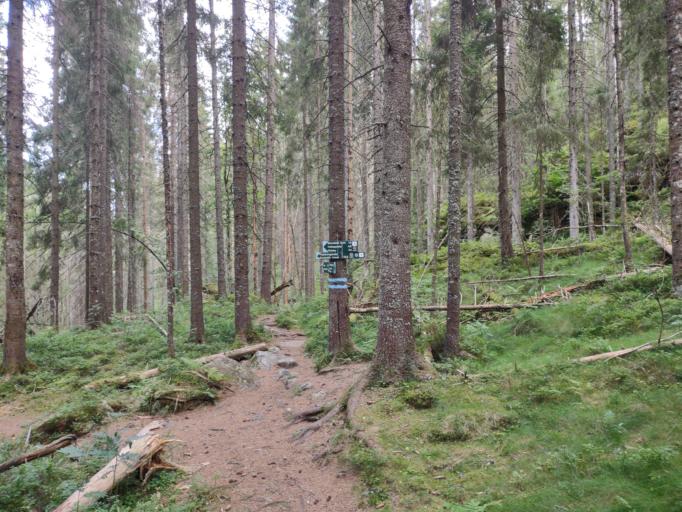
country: NO
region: Akershus
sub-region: Raelingen
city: Fjerdingby
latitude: 59.8181
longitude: 11.0283
